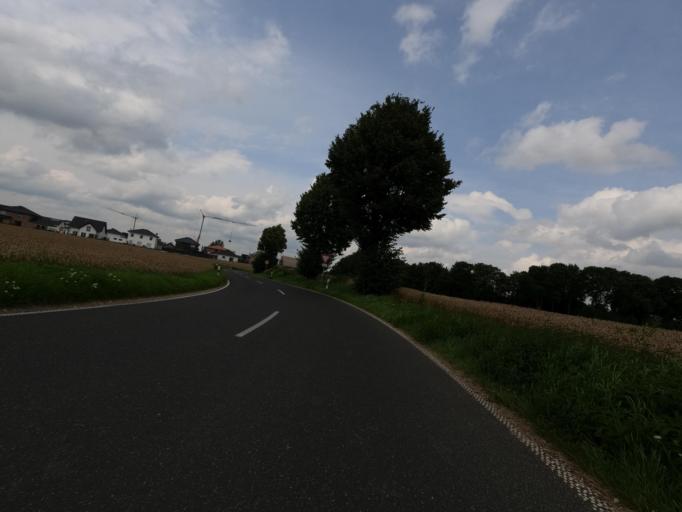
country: DE
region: North Rhine-Westphalia
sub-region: Regierungsbezirk Koln
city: Linnich
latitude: 50.9922
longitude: 6.2141
